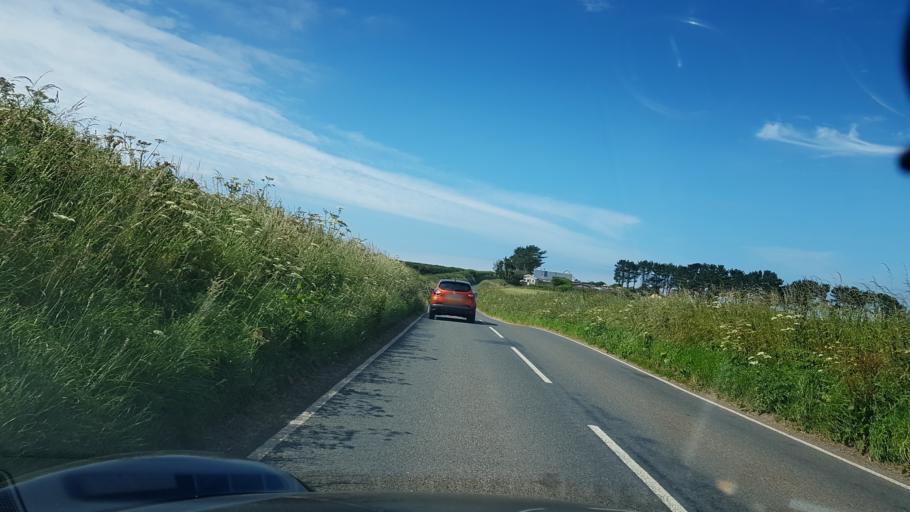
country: GB
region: Wales
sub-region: Pembrokeshire
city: Herbrandston
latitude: 51.7579
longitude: -5.1088
